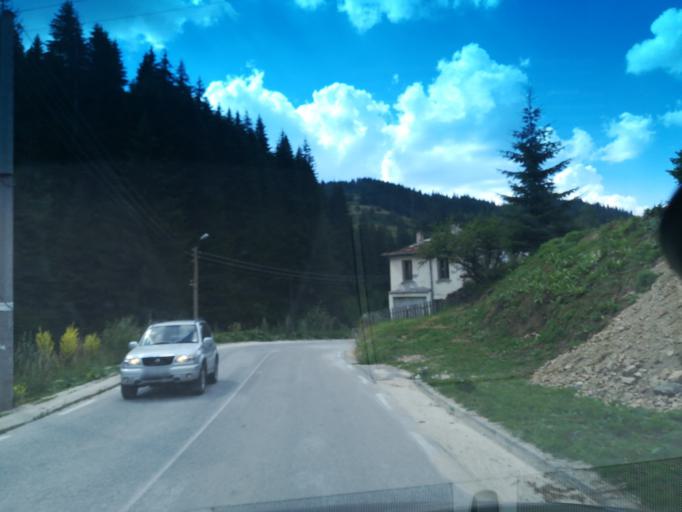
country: BG
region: Smolyan
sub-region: Obshtina Smolyan
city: Smolyan
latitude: 41.6553
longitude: 24.6351
